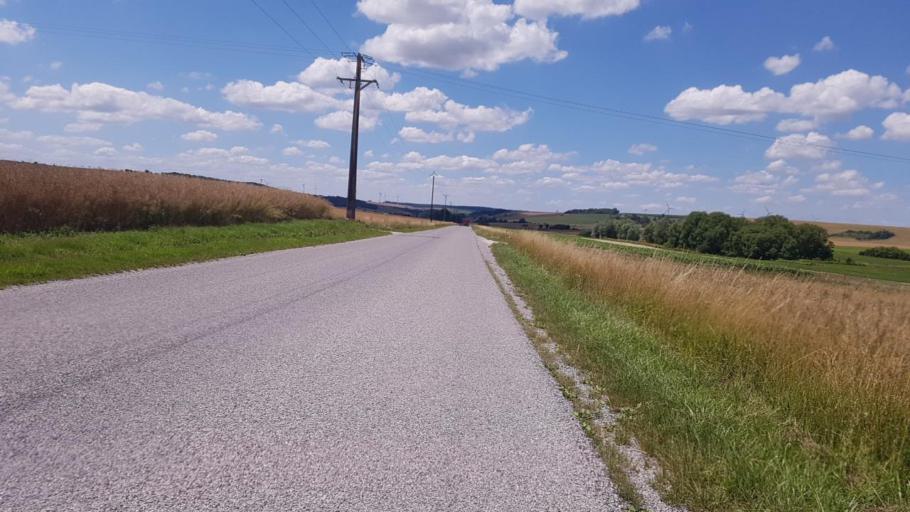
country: FR
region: Lorraine
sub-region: Departement de la Meuse
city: Vacon
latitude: 48.6536
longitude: 5.5324
